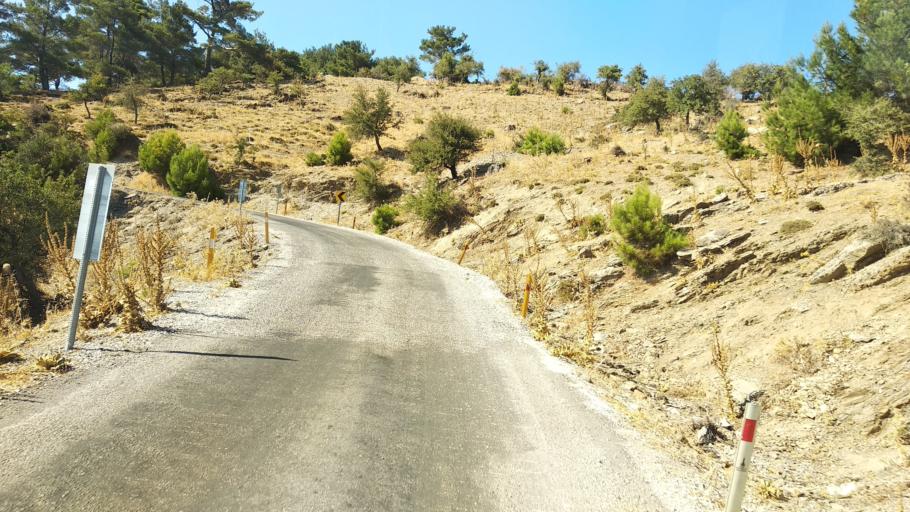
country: TR
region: Izmir
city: Gaziemir
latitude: 38.2955
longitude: 27.0006
